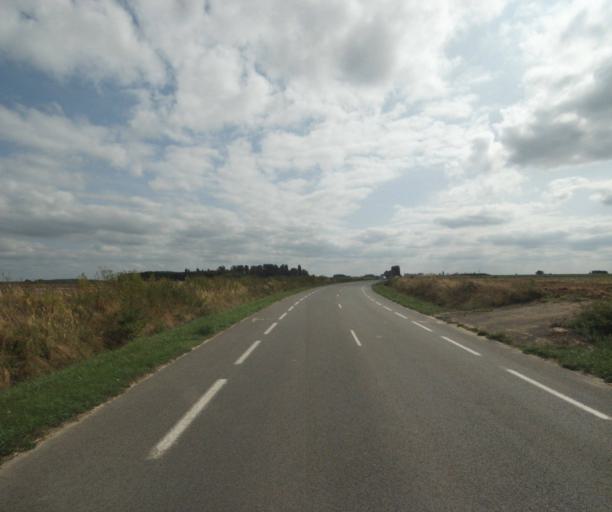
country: FR
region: Nord-Pas-de-Calais
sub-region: Departement du Nord
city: Gruson
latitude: 50.5974
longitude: 3.2300
